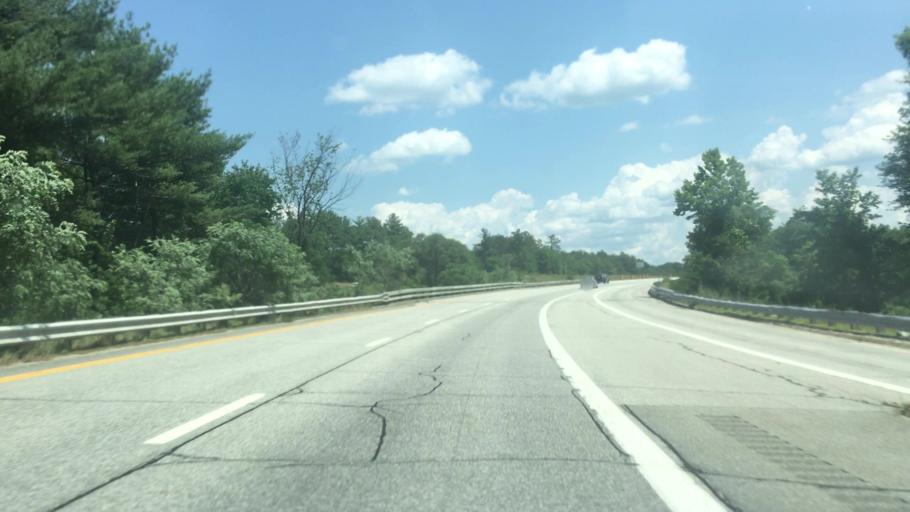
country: US
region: New Hampshire
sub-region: Merrimack County
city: Contoocook
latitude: 43.2726
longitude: -71.7890
